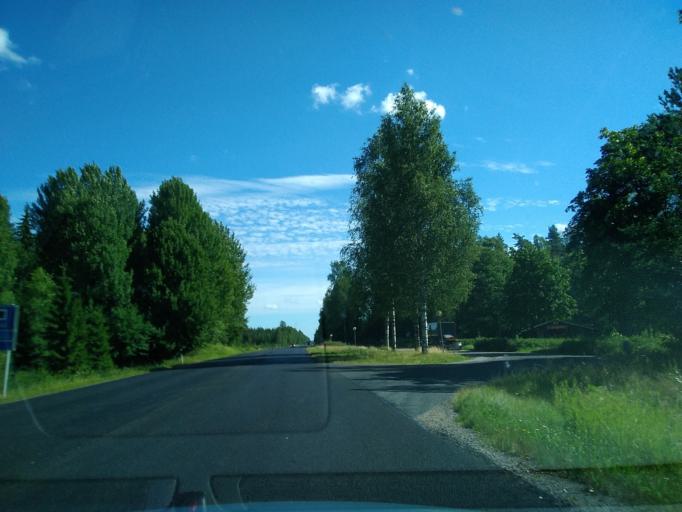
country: FI
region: Haeme
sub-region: Haemeenlinna
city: Renko
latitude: 60.9250
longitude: 24.3430
